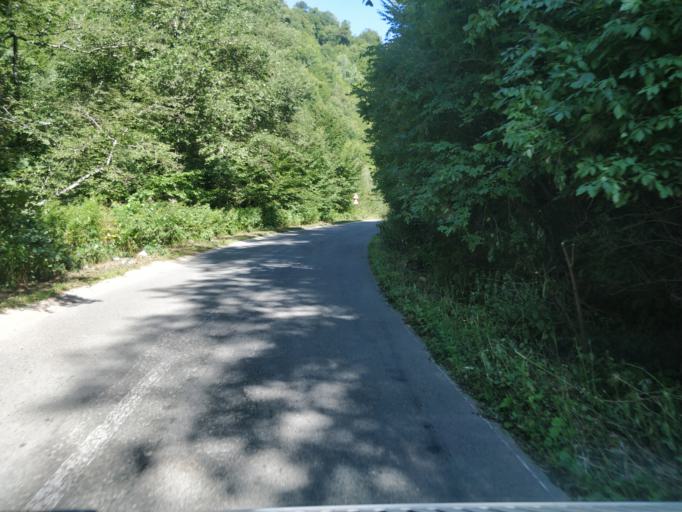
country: RO
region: Cluj
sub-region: Comuna Sacueu
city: Sacuieu
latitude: 46.8422
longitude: 22.8611
